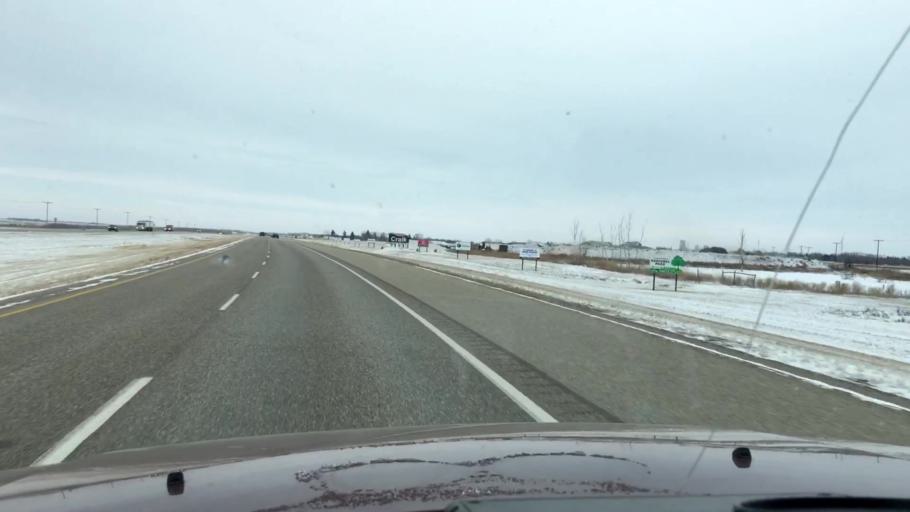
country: CA
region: Saskatchewan
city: Watrous
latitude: 51.0654
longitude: -105.8336
